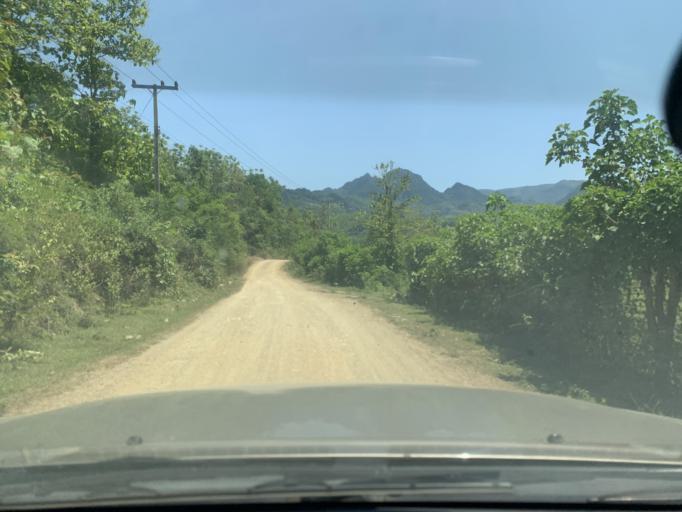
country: LA
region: Louangphabang
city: Louangphabang
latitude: 19.9043
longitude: 102.2511
